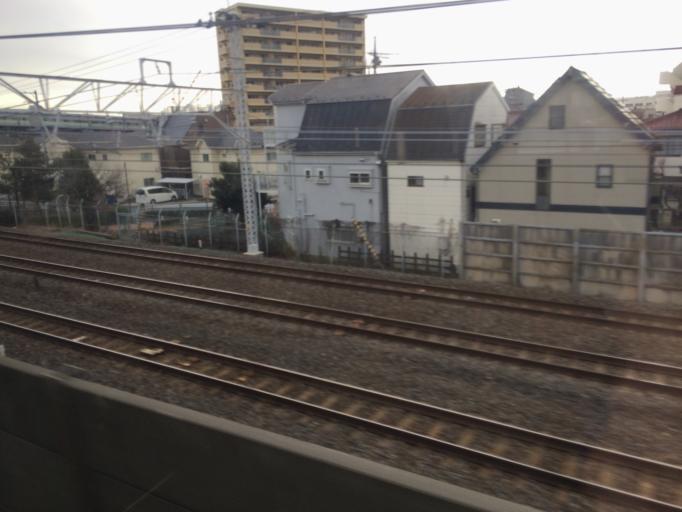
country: JP
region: Tokyo
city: Urayasu
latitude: 35.7254
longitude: 139.8701
